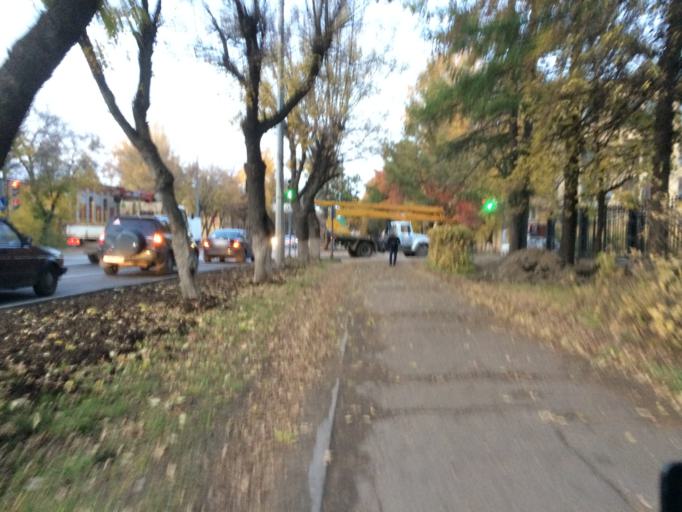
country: RU
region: Mariy-El
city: Yoshkar-Ola
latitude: 56.6137
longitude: 47.8821
